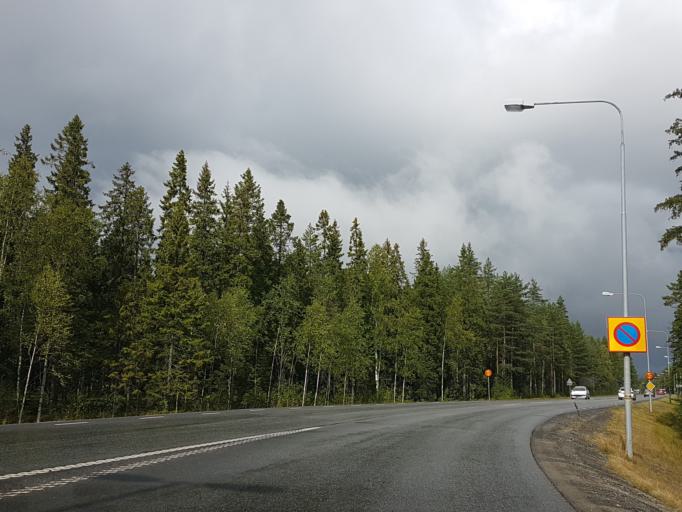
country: SE
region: Vaesterbotten
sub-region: Umea Kommun
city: Ersmark
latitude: 63.8478
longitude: 20.3422
